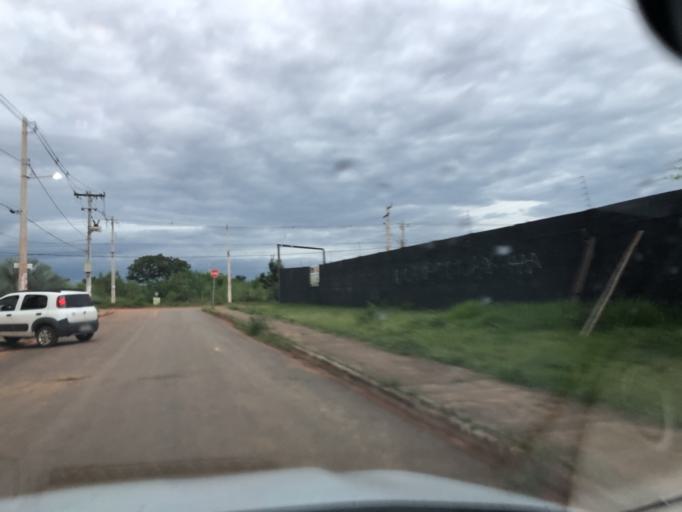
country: BR
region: Goias
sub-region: Luziania
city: Luziania
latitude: -16.1074
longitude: -47.9750
